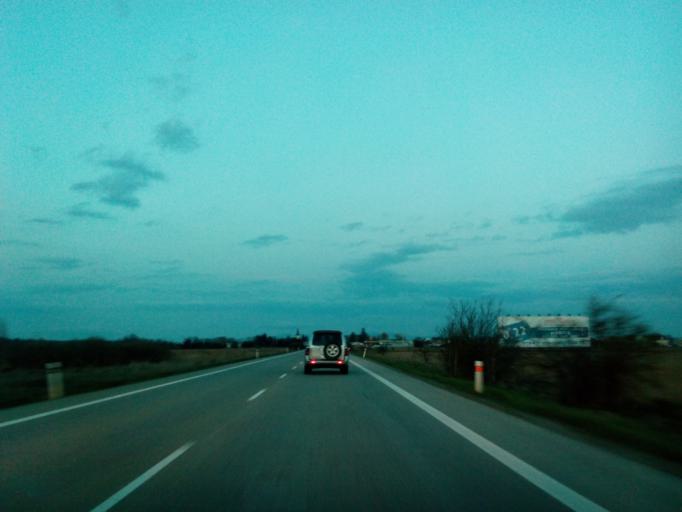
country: SK
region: Kosicky
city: Moldava nad Bodvou
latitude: 48.5979
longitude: 21.0518
